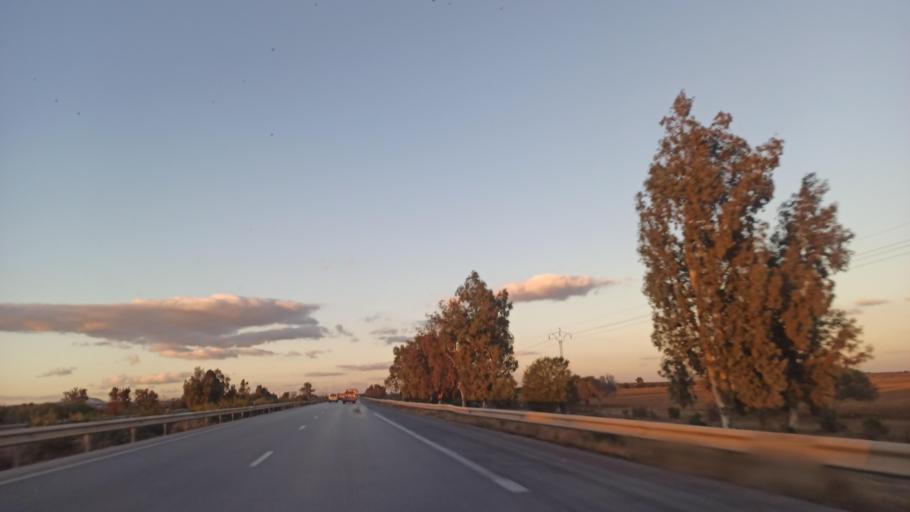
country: TN
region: Susah
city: Harqalah
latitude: 36.1246
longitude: 10.4060
